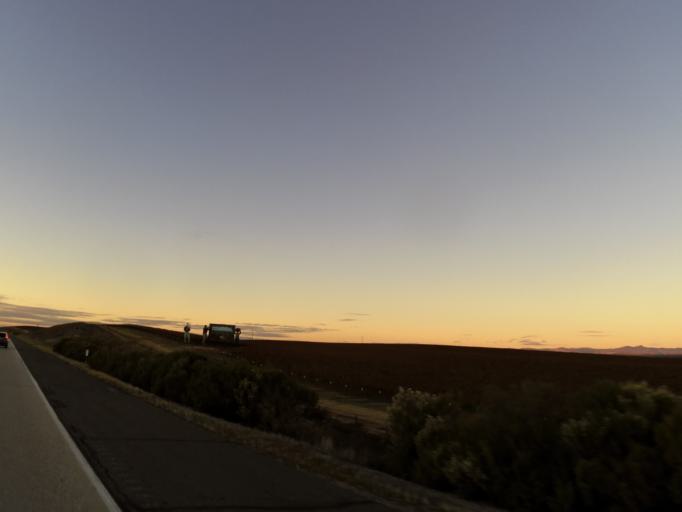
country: US
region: California
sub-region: Monterey County
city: King City
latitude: 36.0659
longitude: -120.9842
